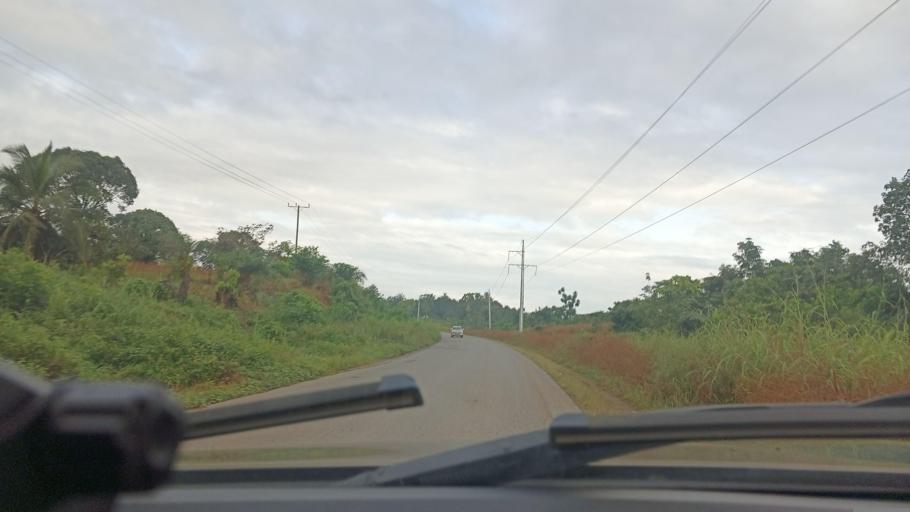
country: LR
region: Montserrado
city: Monrovia
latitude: 6.5660
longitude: -10.8736
